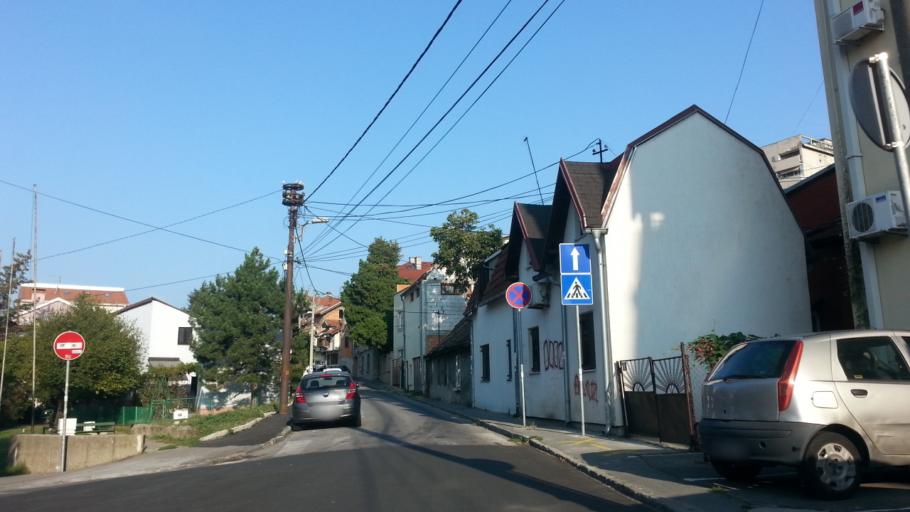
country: RS
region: Central Serbia
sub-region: Belgrade
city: Vracar
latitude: 44.7950
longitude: 20.4810
